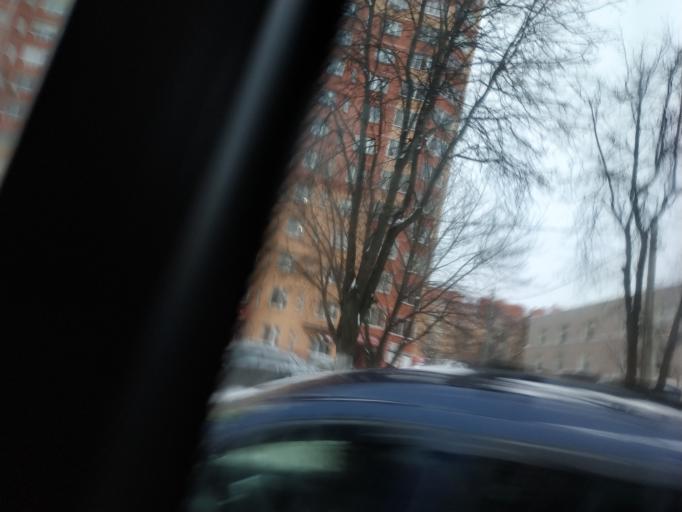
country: RU
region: Moskovskaya
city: Shchelkovo
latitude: 55.9277
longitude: 37.9870
